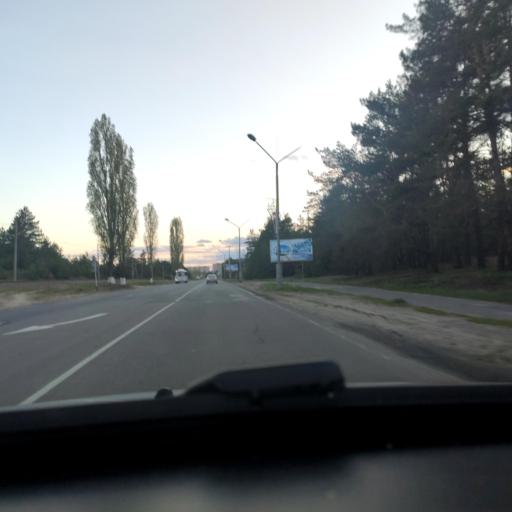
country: RU
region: Voronezj
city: Novovoronezh
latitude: 51.3251
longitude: 39.2383
